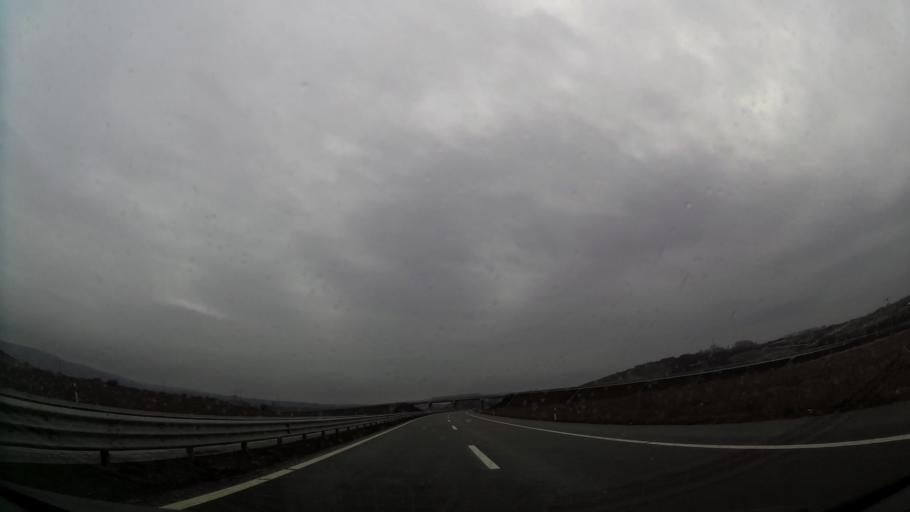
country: XK
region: Ferizaj
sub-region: Komuna e Ferizajt
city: Ferizaj
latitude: 42.4439
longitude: 21.1965
